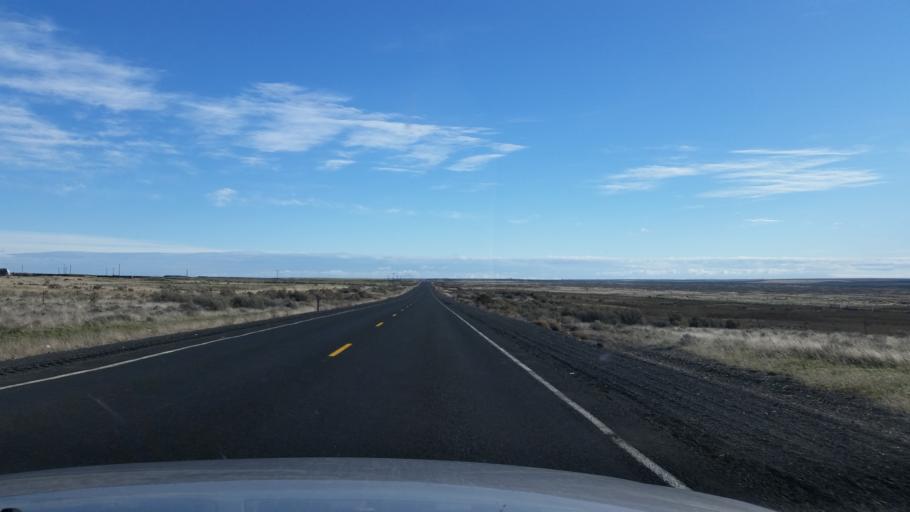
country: US
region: Washington
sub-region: Grant County
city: Warden
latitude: 47.3440
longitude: -118.9176
